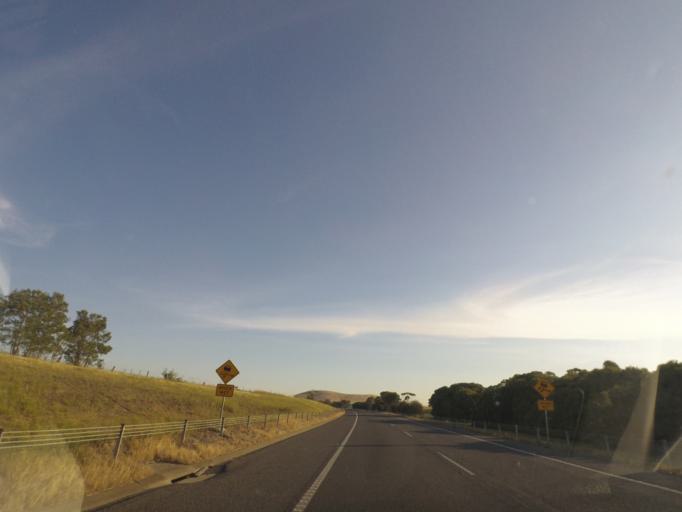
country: AU
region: Victoria
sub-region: Whittlesea
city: Whittlesea
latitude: -37.4362
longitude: 144.9818
